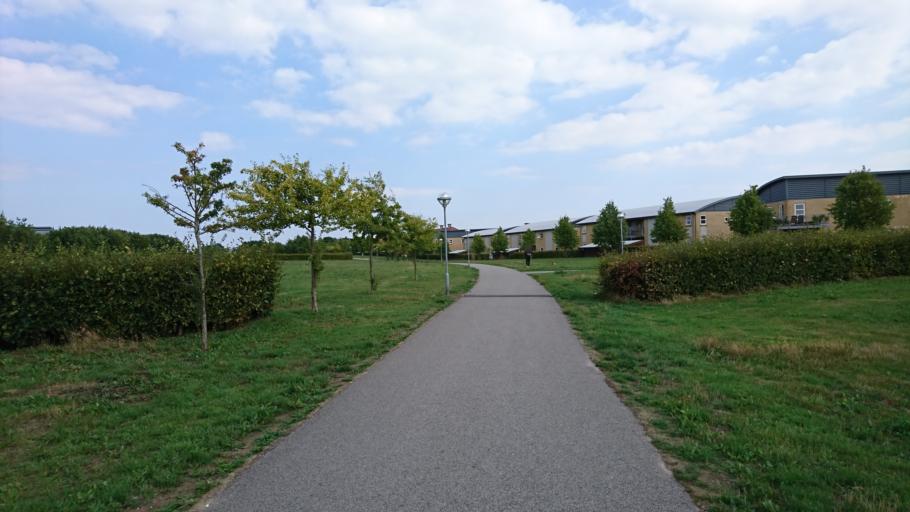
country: DK
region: Capital Region
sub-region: Egedal Kommune
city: Smorumnedre
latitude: 55.7474
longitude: 12.2915
